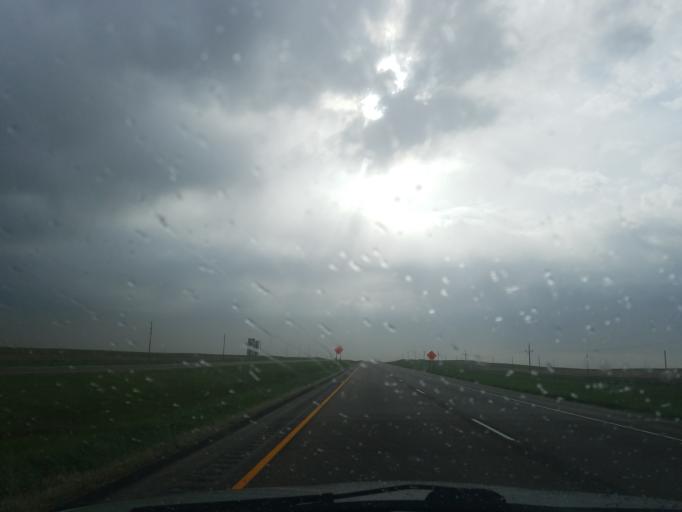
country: US
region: North Dakota
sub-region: Burleigh County
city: Lincoln
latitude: 46.8363
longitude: -100.3142
